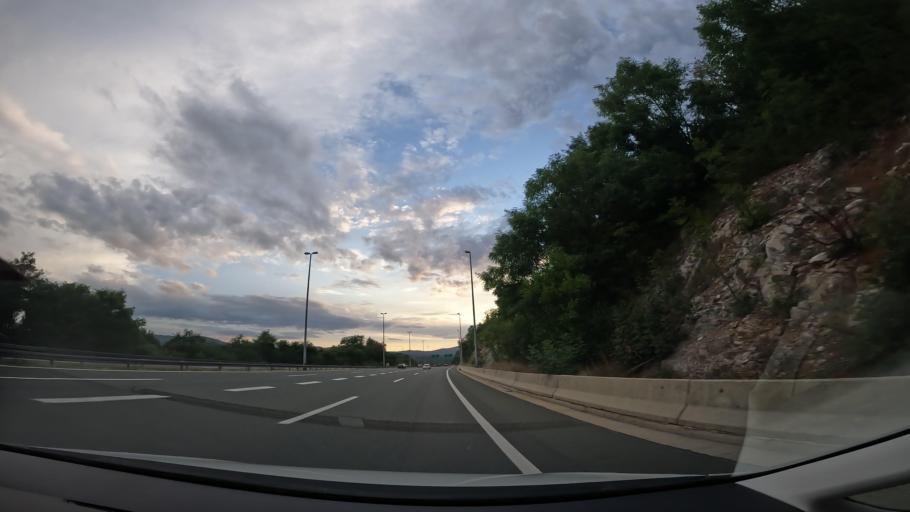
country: HR
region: Karlovacka
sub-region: Grad Ogulin
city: Ogulin
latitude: 45.4108
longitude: 15.2718
